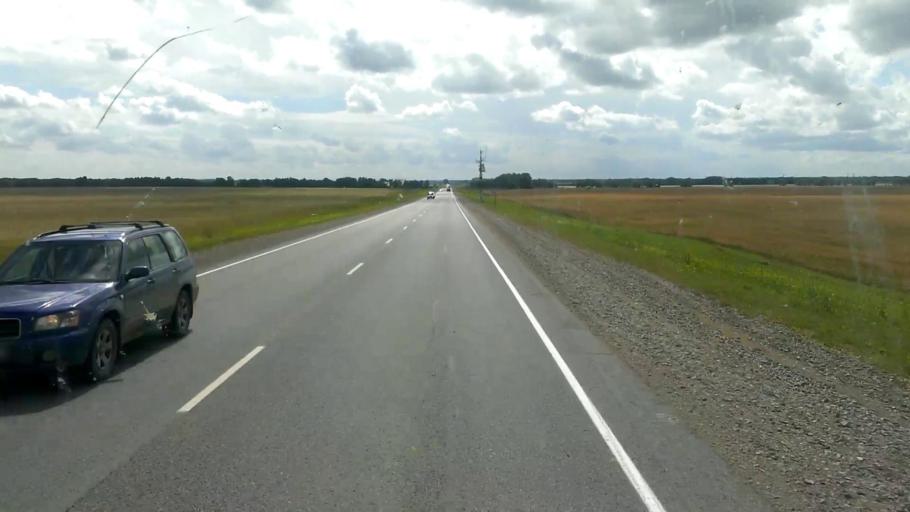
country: RU
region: Altai Krai
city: Troitskoye
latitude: 52.9007
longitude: 84.8323
